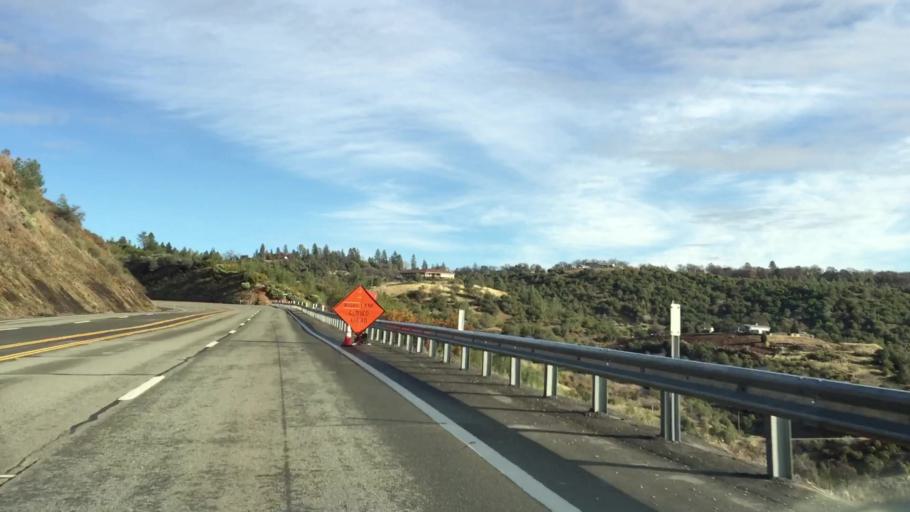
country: US
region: California
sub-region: Butte County
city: Paradise
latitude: 39.6949
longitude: -121.5313
